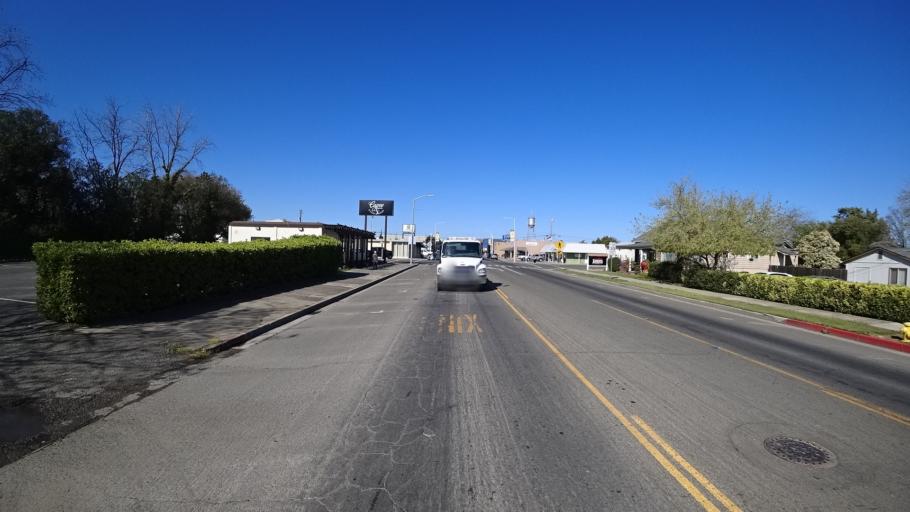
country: US
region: California
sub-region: Glenn County
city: Orland
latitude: 39.7474
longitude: -122.1921
